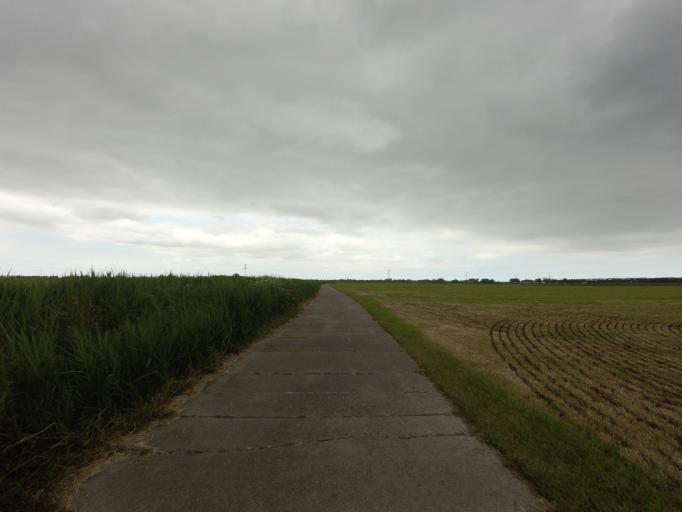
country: NL
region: North Holland
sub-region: Gemeente Hoorn
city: Hoorn
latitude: 52.6578
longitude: 5.0236
